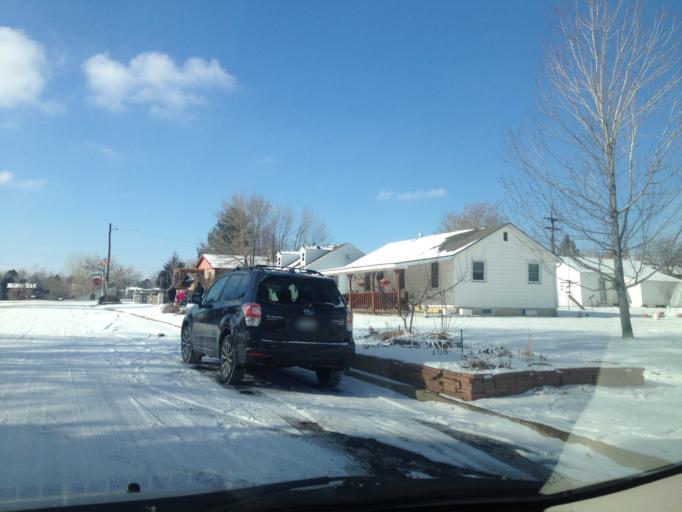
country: US
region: Colorado
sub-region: Boulder County
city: Lafayette
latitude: 39.9973
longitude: -105.0946
